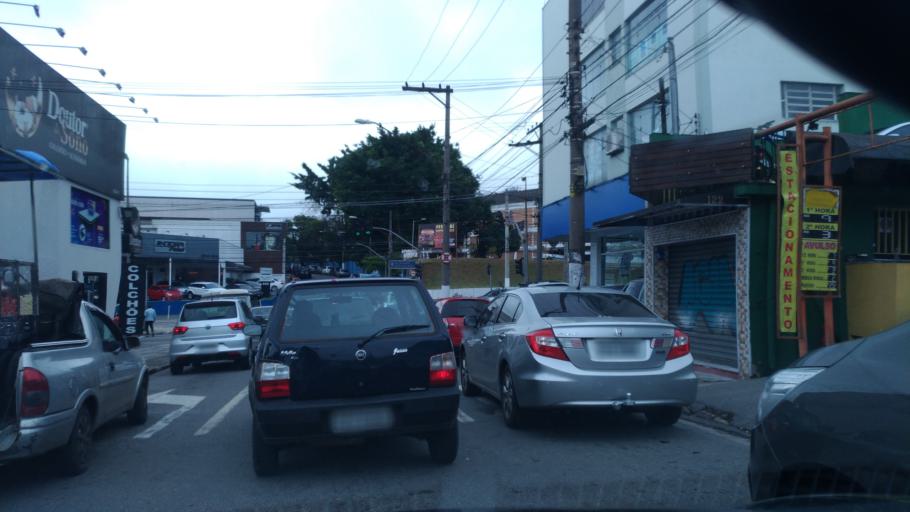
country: BR
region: Sao Paulo
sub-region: Sao Bernardo Do Campo
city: Sao Bernardo do Campo
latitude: -23.6915
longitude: -46.5581
